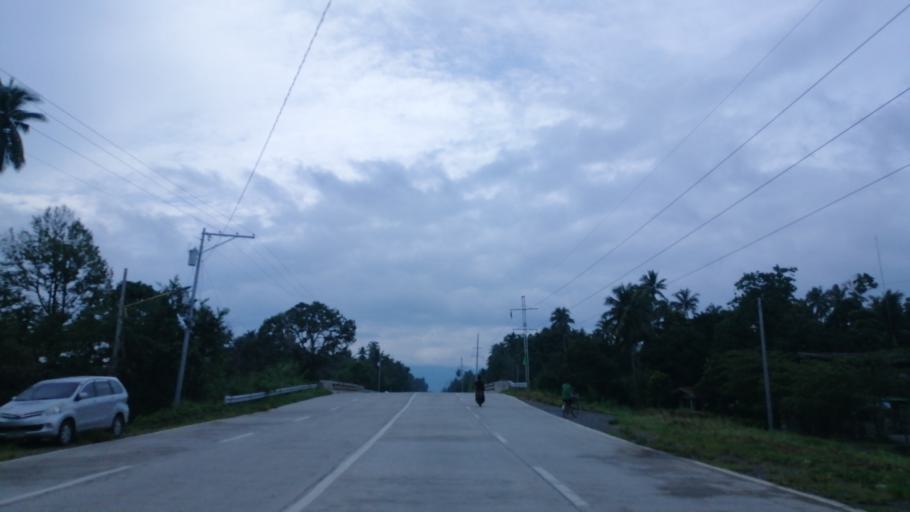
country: PH
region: Davao
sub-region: Province of Davao del Norte
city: Corocotan
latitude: 7.3959
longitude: 125.7805
